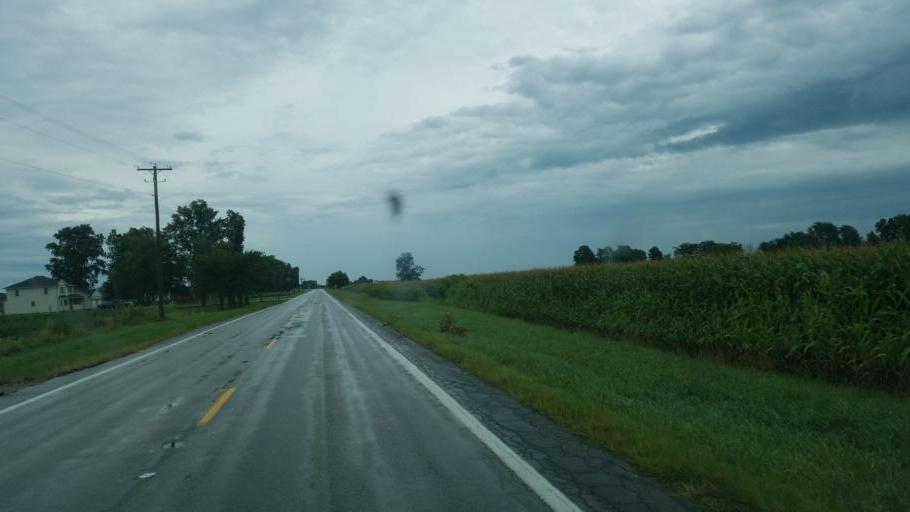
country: US
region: Ohio
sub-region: Delaware County
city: Delaware
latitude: 40.3251
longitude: -83.0149
